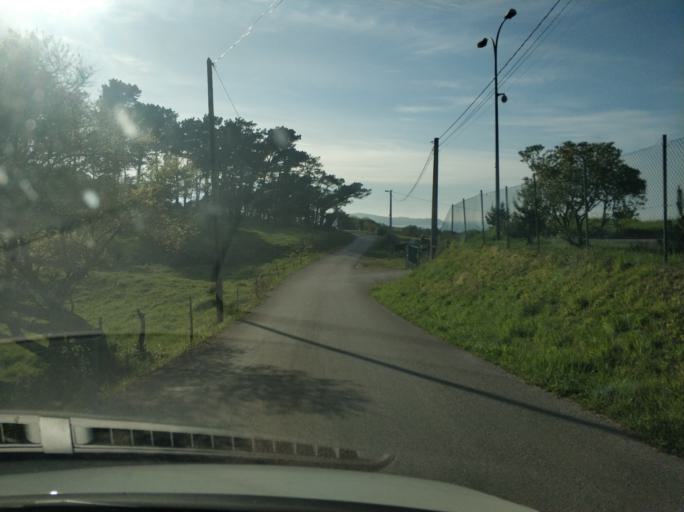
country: ES
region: Cantabria
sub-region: Provincia de Cantabria
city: Comillas
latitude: 43.3890
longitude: -4.3009
